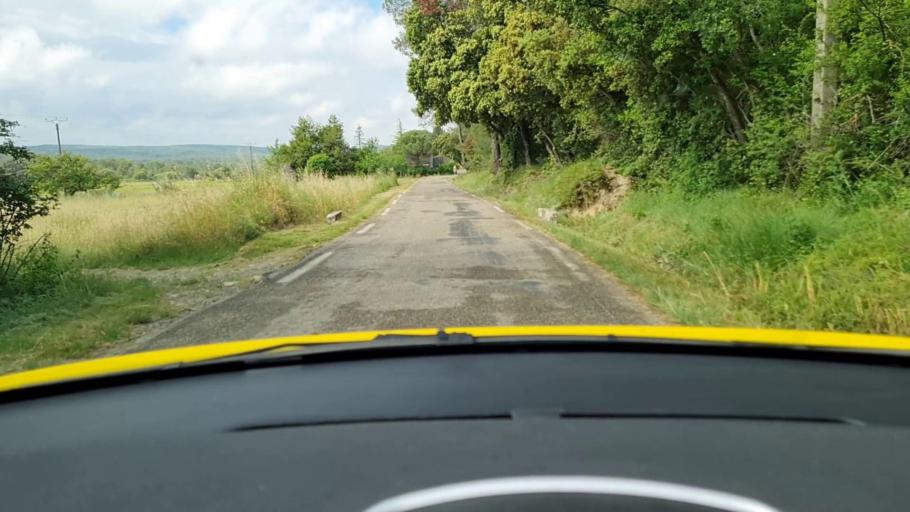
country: FR
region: Languedoc-Roussillon
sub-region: Departement du Gard
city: Quissac
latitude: 43.8445
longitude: 4.0030
